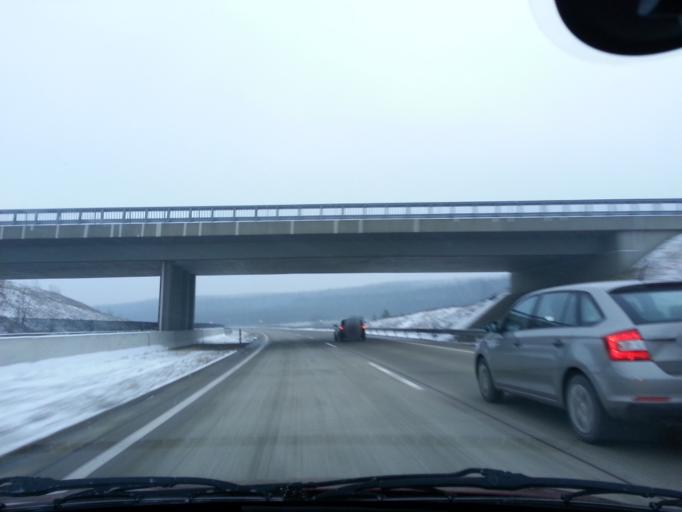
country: HU
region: Pest
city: Kerepes
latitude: 47.5849
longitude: 19.3124
